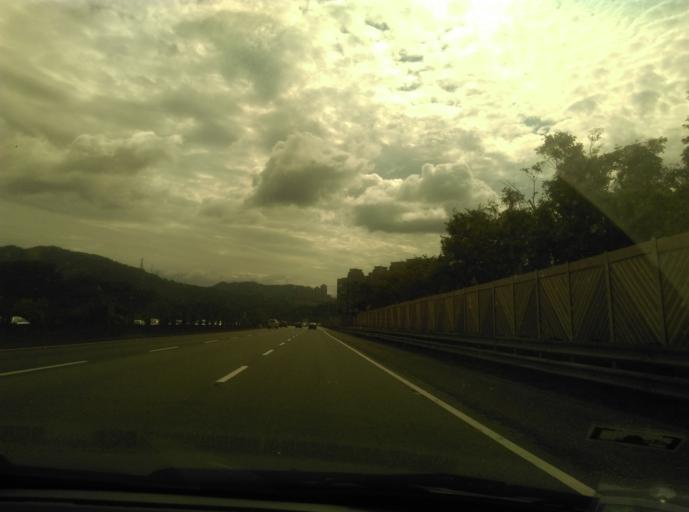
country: TW
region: Taipei
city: Taipei
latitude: 25.0653
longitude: 121.6432
